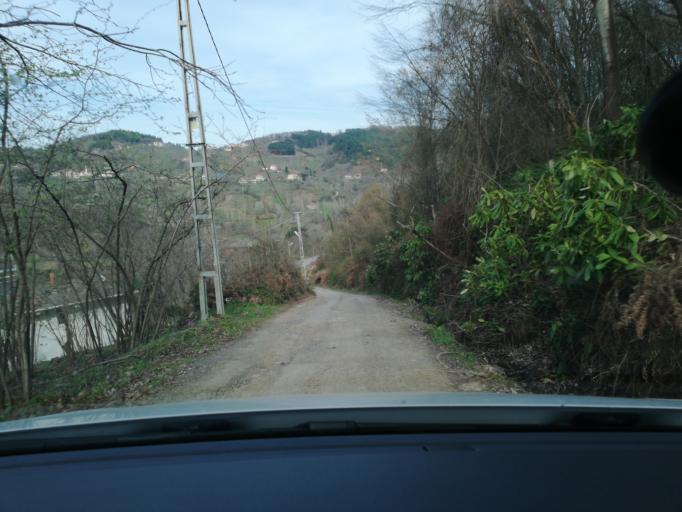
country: TR
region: Zonguldak
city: Kozlu
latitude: 41.3602
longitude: 31.6265
